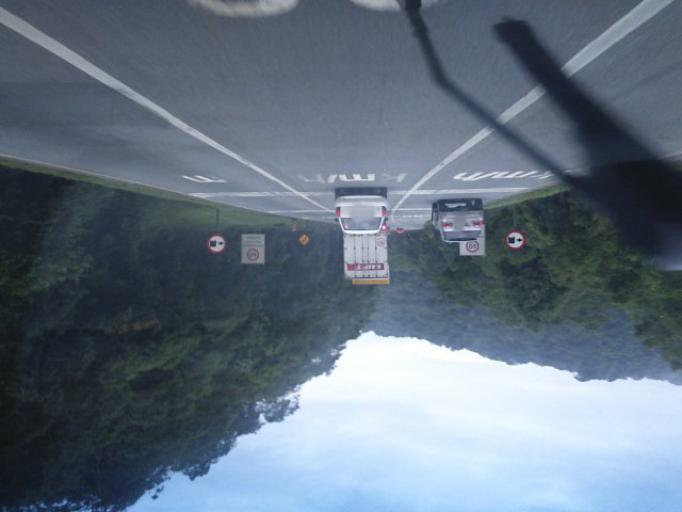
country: BR
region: Parana
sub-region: Guaratuba
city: Guaratuba
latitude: -25.8551
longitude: -48.9548
